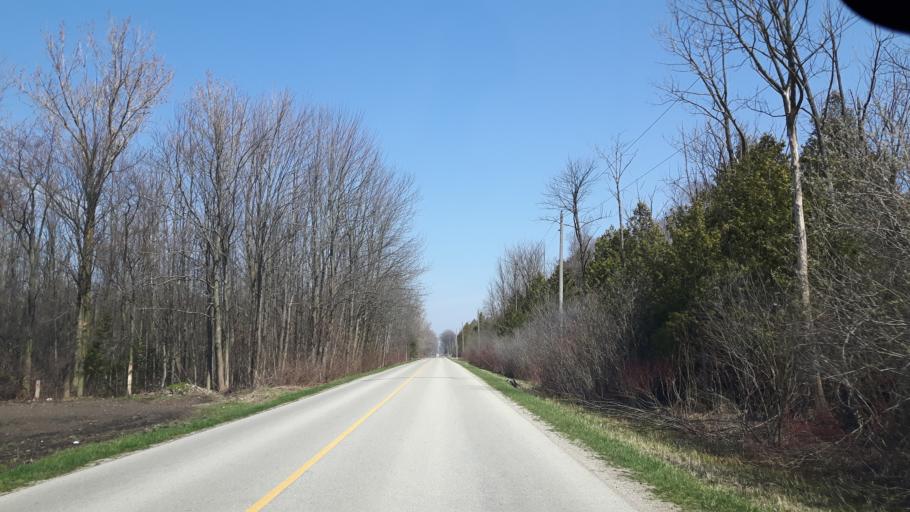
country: CA
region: Ontario
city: Goderich
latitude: 43.6870
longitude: -81.6847
